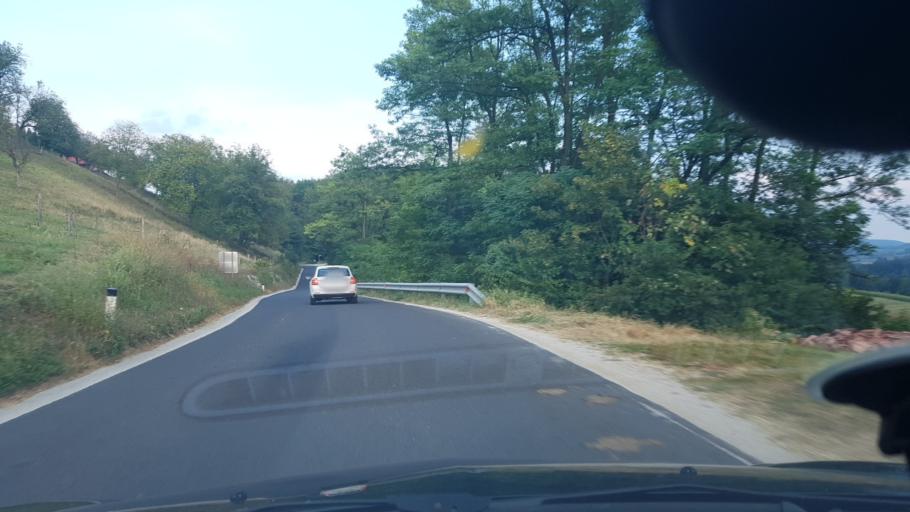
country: SI
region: Kozje
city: Kozje
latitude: 46.1054
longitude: 15.5889
